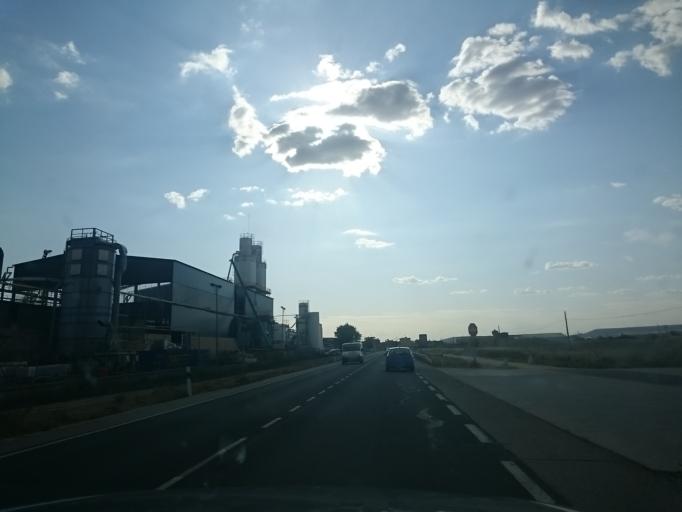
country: ES
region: Castille and Leon
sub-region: Provincia de Burgos
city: Cardenajimeno
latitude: 42.3428
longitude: -3.6198
